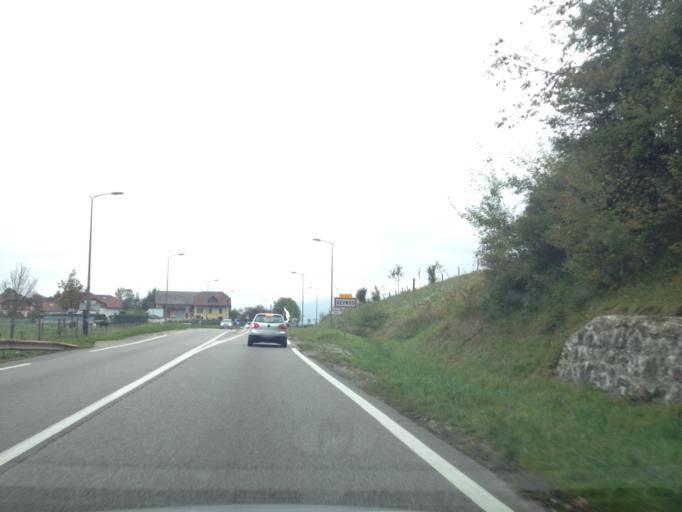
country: FR
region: Rhone-Alpes
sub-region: Departement de la Haute-Savoie
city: Seynod
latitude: 45.8750
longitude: 6.0820
